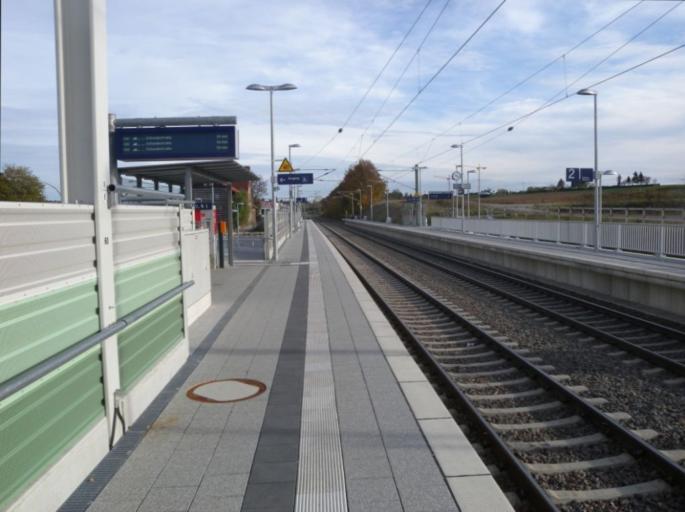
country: DE
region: Baden-Wuerttemberg
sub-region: Regierungsbezirk Stuttgart
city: Magstadt
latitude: 48.7365
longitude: 8.9648
